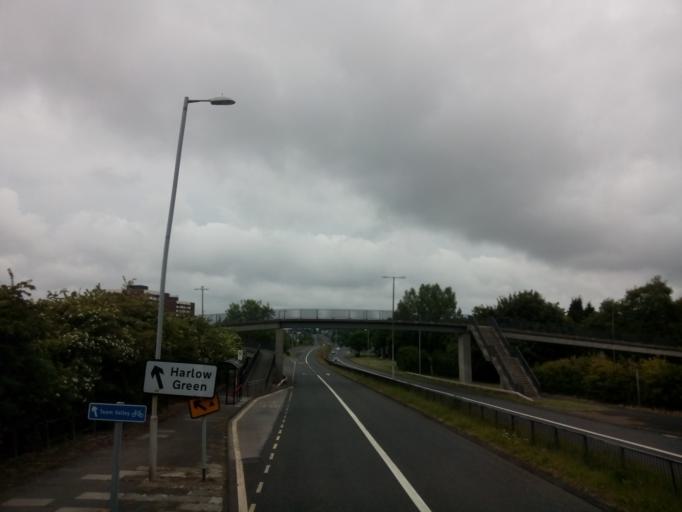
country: GB
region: England
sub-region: Gateshead
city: Lamesley
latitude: 54.9179
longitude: -1.5899
